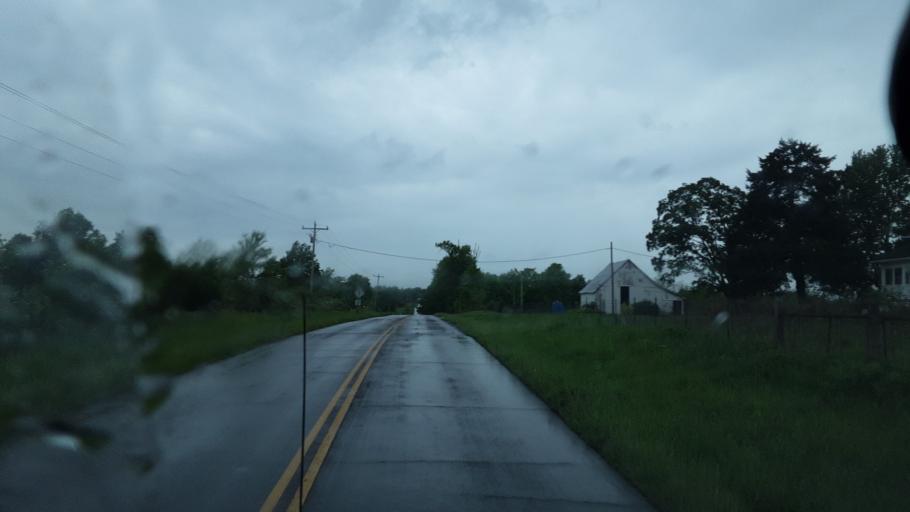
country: US
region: Missouri
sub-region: Boone County
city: Centralia
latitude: 39.3884
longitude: -92.2218
